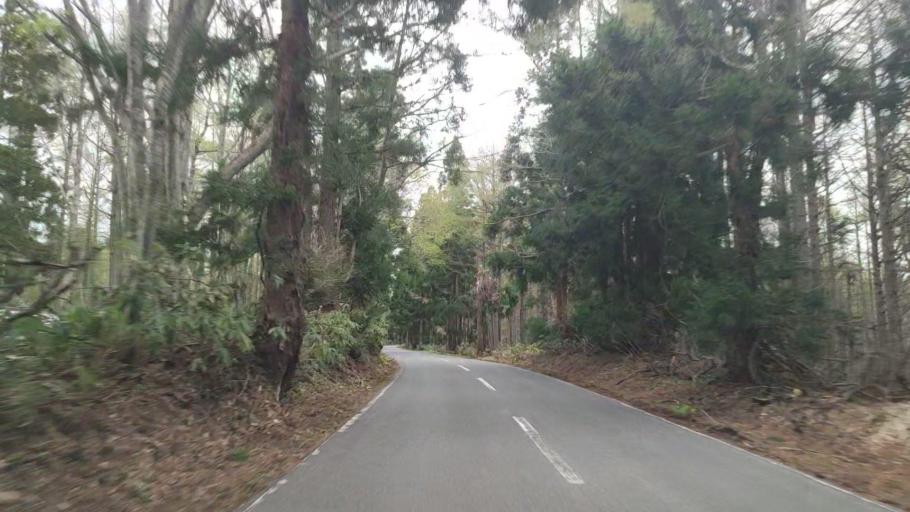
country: JP
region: Aomori
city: Aomori Shi
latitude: 40.7230
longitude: 140.8536
